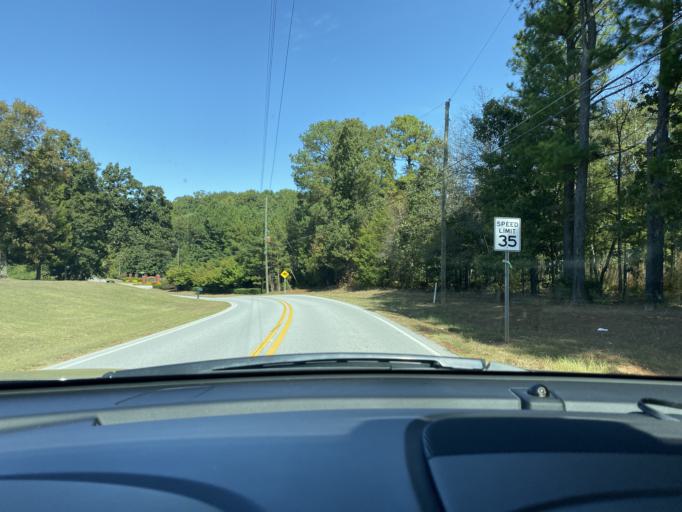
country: US
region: Georgia
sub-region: Walton County
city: Loganville
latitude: 33.8840
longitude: -83.9079
